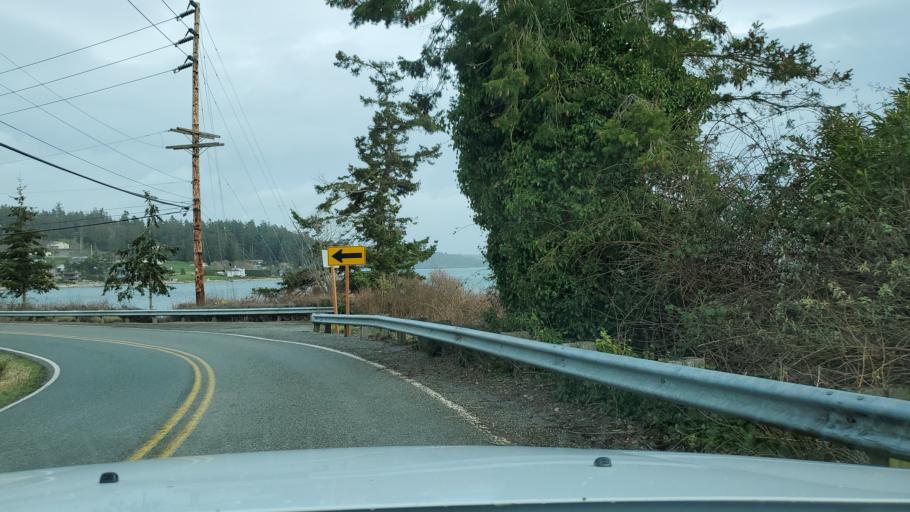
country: US
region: Washington
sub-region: Skagit County
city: Anacortes
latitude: 48.4226
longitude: -122.6110
